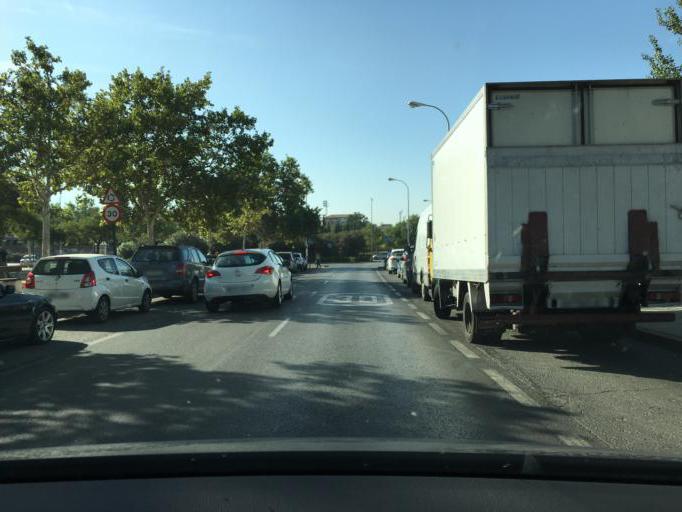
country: ES
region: Andalusia
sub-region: Provincia de Granada
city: Granada
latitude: 37.1988
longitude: -3.6078
